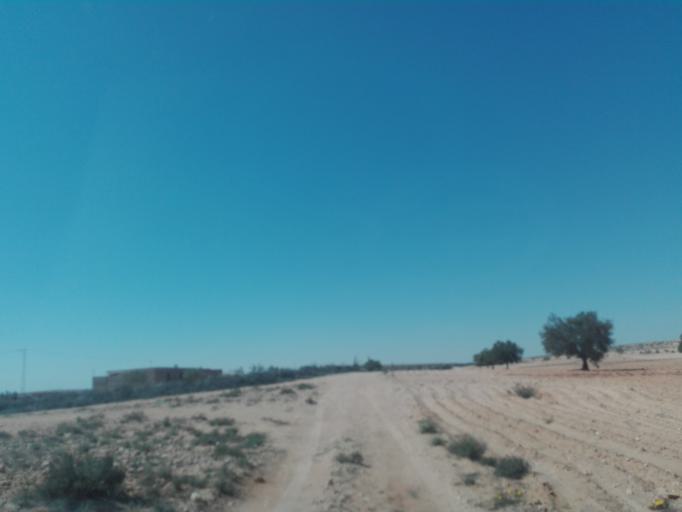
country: TN
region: Safaqis
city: Bi'r `Ali Bin Khalifah
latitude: 34.7942
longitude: 10.2819
